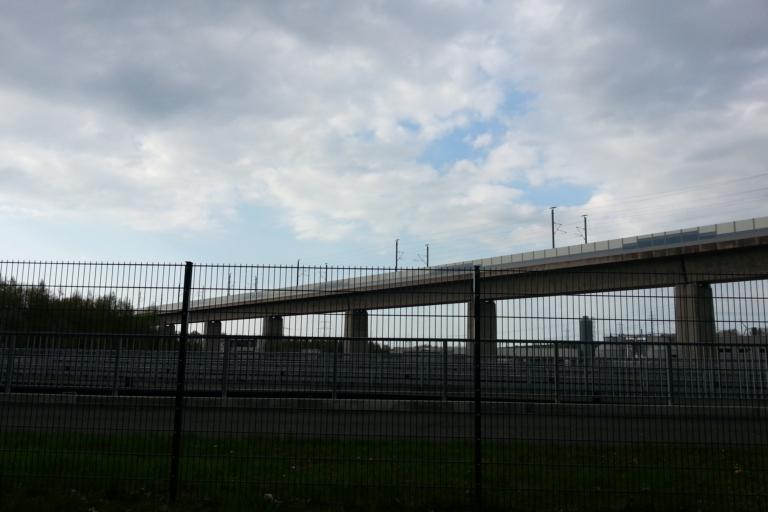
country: DE
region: Thuringia
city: Ichtershausen
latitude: 50.8879
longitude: 10.9723
